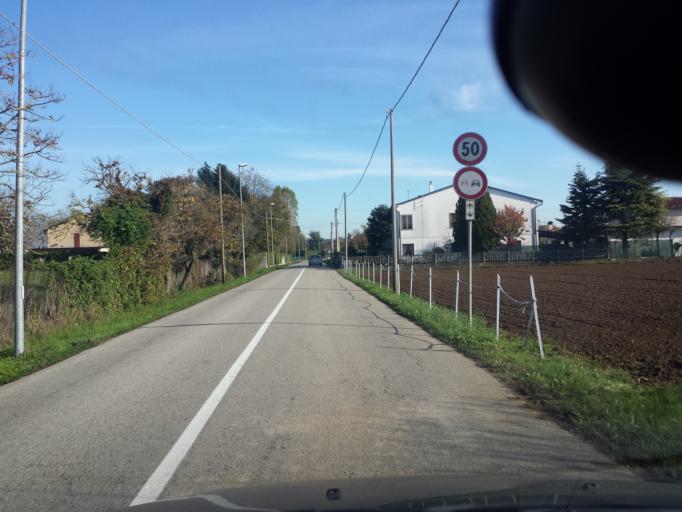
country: IT
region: Veneto
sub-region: Provincia di Vicenza
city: Dueville
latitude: 45.6221
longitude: 11.5635
